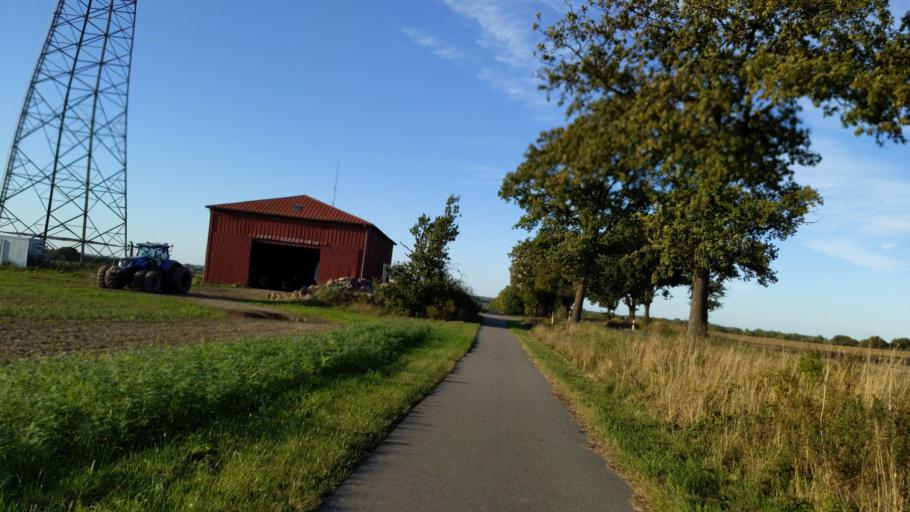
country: DE
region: Schleswig-Holstein
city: Ahrensbok
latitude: 54.0396
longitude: 10.5612
